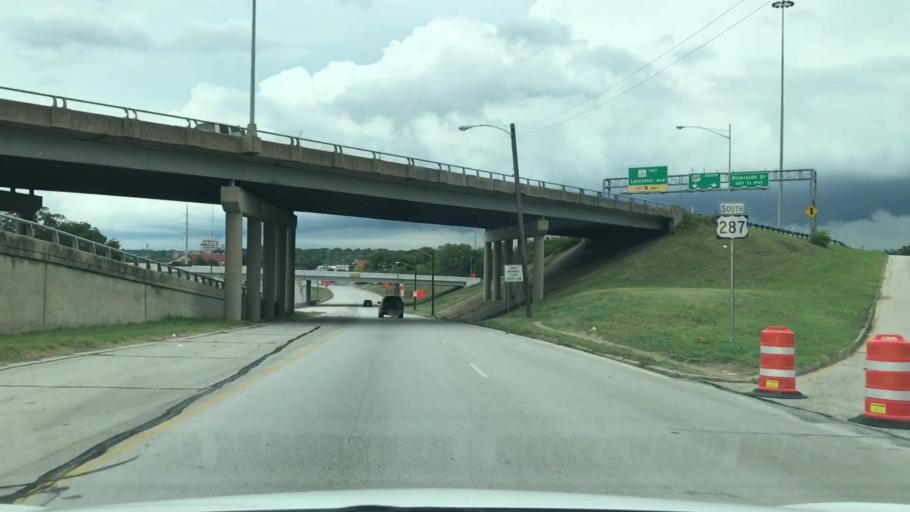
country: US
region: Texas
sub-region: Tarrant County
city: Fort Worth
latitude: 32.7461
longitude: -97.3083
